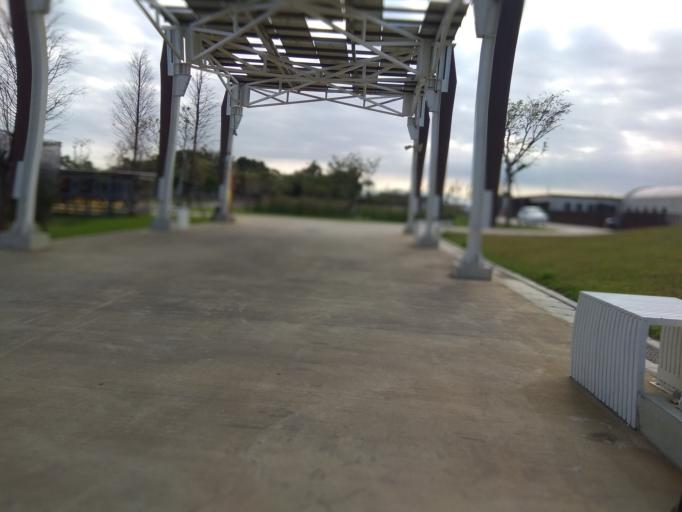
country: TW
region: Taiwan
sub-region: Hsinchu
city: Zhubei
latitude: 25.0079
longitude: 121.0490
